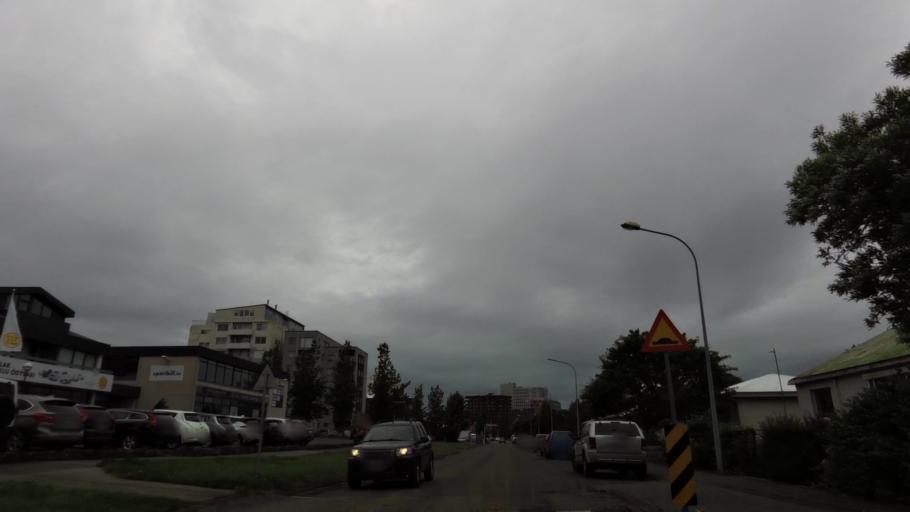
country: IS
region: Capital Region
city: Reykjavik
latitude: 64.1424
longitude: -21.8991
